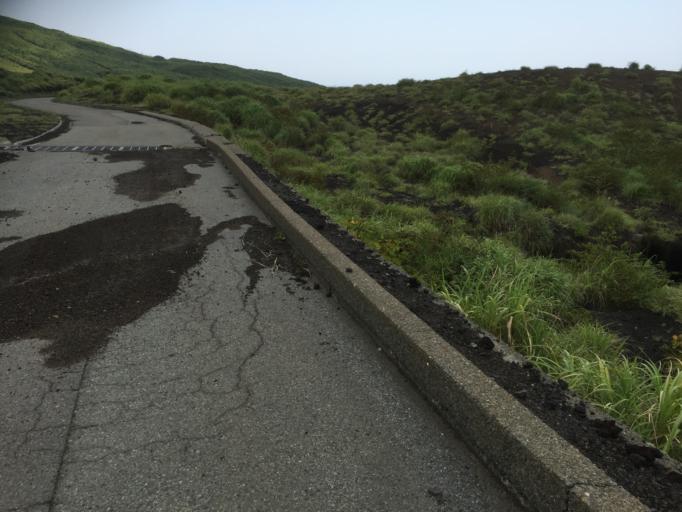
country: JP
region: Shizuoka
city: Shimoda
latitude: 34.0714
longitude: 139.5139
